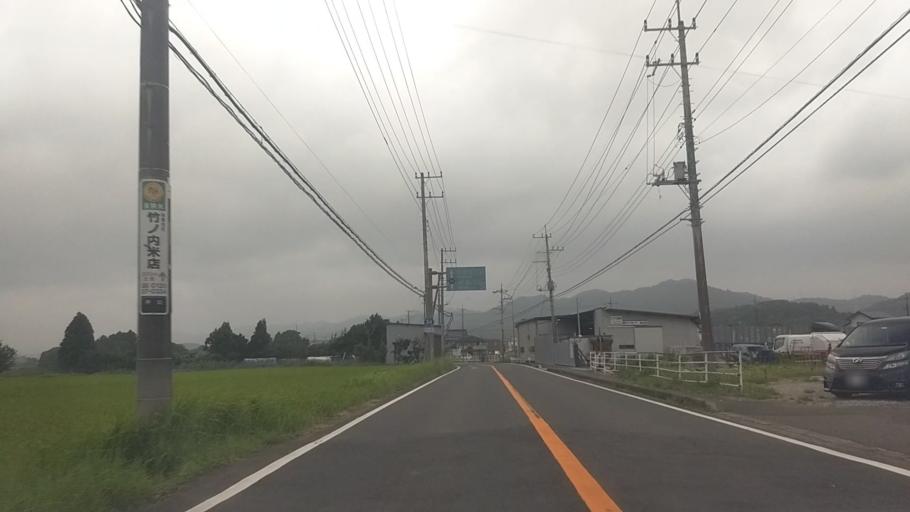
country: JP
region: Chiba
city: Kawaguchi
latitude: 35.1243
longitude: 140.0602
